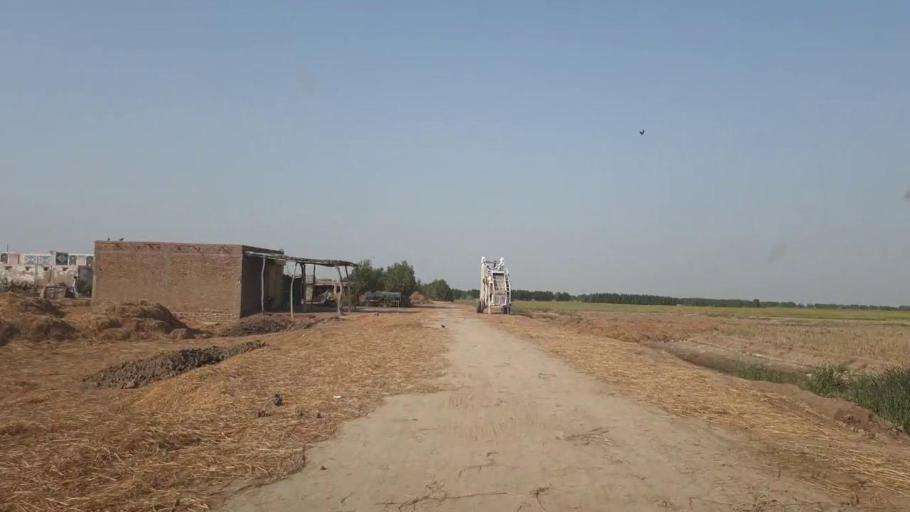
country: PK
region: Sindh
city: Kario
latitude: 24.5781
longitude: 68.5441
